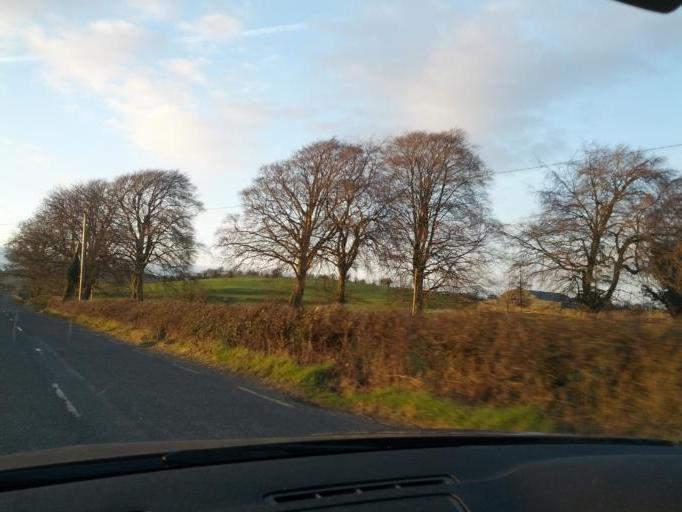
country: IE
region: Munster
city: Nenagh Bridge
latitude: 52.9568
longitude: -8.2347
